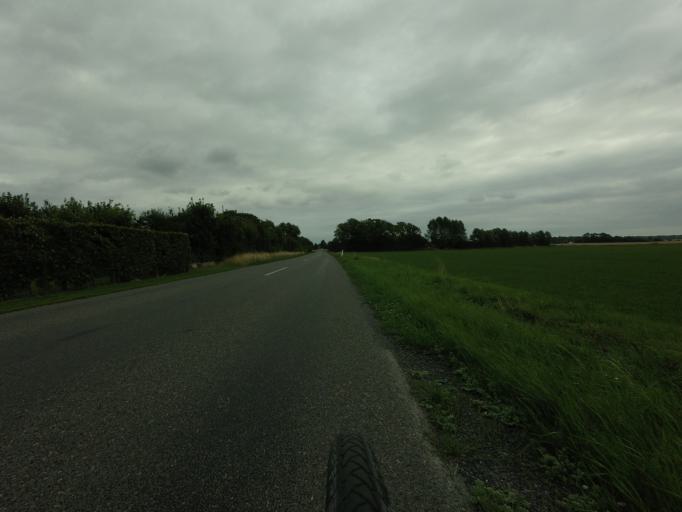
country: DK
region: Zealand
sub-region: Stevns Kommune
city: Store Heddinge
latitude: 55.3450
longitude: 12.3330
